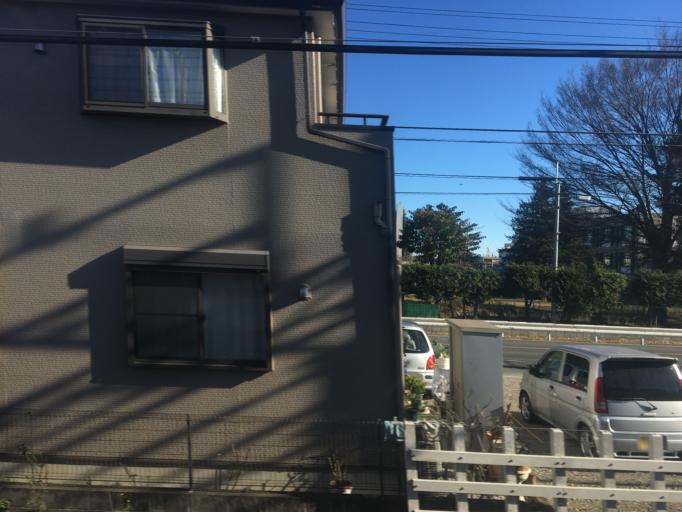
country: JP
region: Saitama
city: Sakado
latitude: 35.9526
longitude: 139.4043
